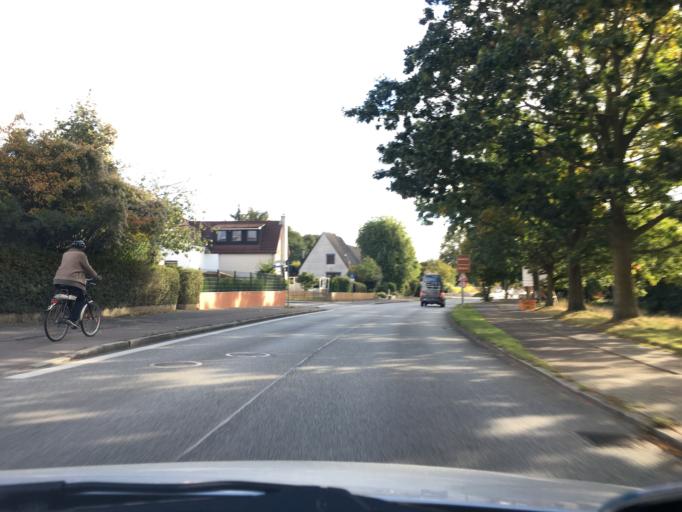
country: DE
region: Schleswig-Holstein
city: Kronshagen
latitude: 54.3000
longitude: 10.0833
